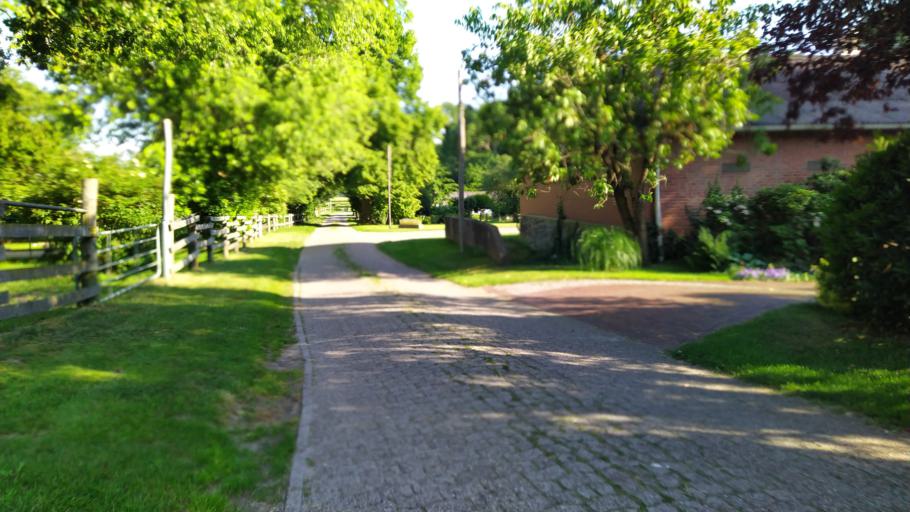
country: DE
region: Lower Saxony
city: Lintig
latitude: 53.5968
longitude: 8.9289
